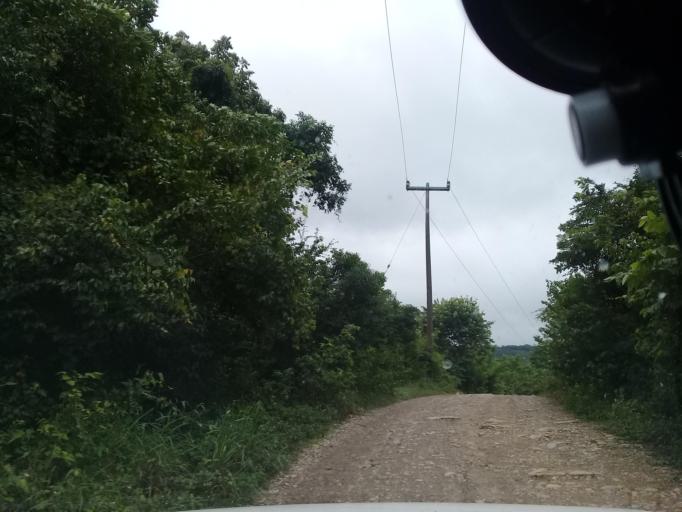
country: MX
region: Veracruz
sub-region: Chalma
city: San Pedro Coyutla
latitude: 21.2395
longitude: -98.4184
